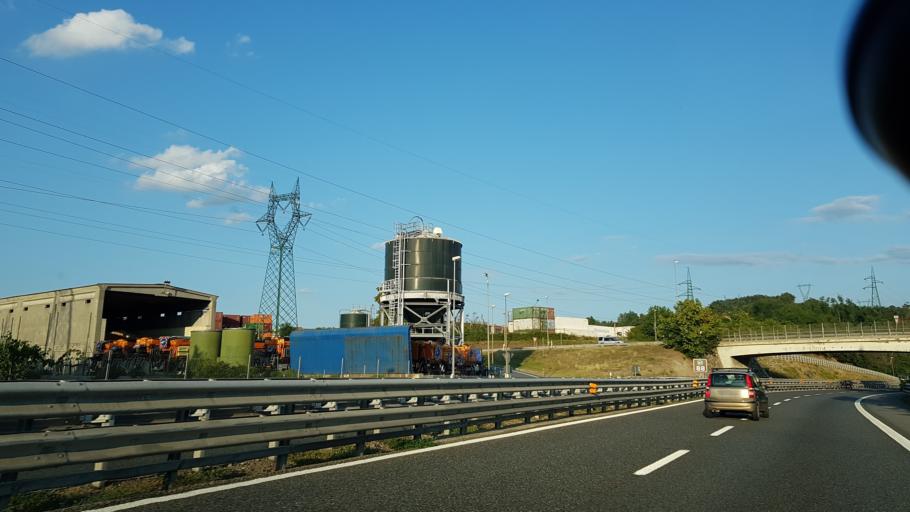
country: IT
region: Piedmont
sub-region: Provincia di Alessandria
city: Vignole Borbera
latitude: 44.7029
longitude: 8.8867
